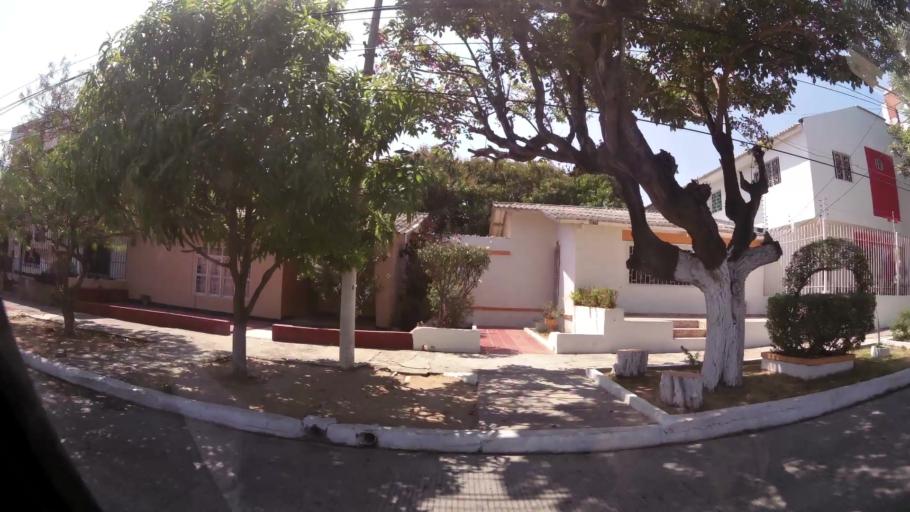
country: CO
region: Atlantico
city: Barranquilla
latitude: 10.9646
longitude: -74.7983
